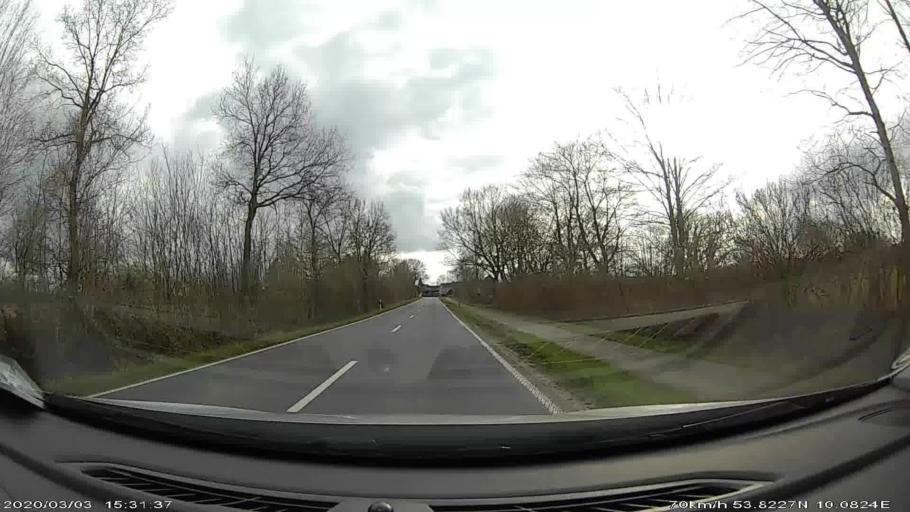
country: DE
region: Schleswig-Holstein
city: Huttblek
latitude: 53.8236
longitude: 10.0829
